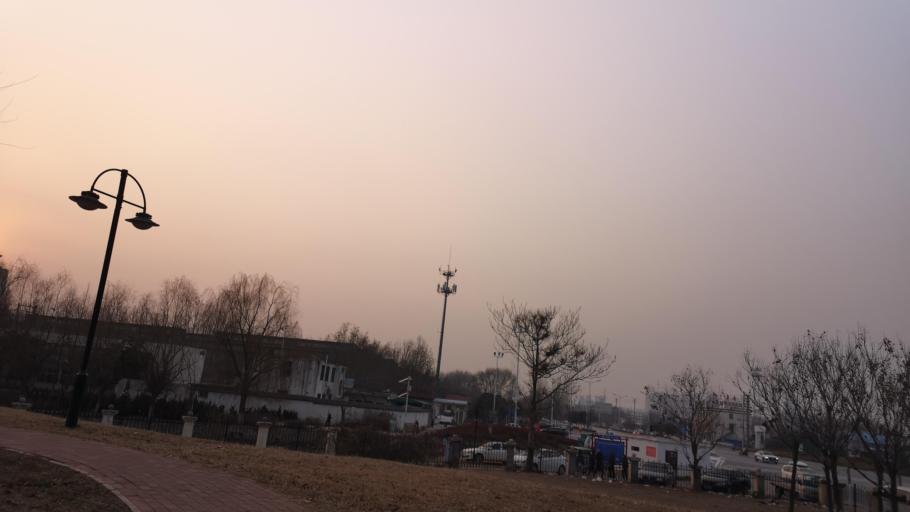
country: CN
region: Henan Sheng
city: Zhongyuanlu
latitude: 35.7895
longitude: 115.0748
